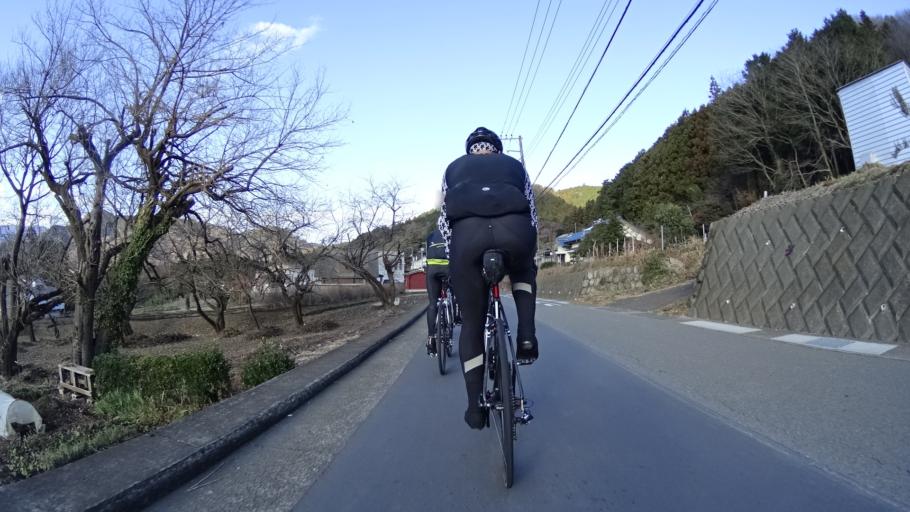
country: JP
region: Tokyo
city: Hachioji
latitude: 35.5701
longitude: 139.2508
